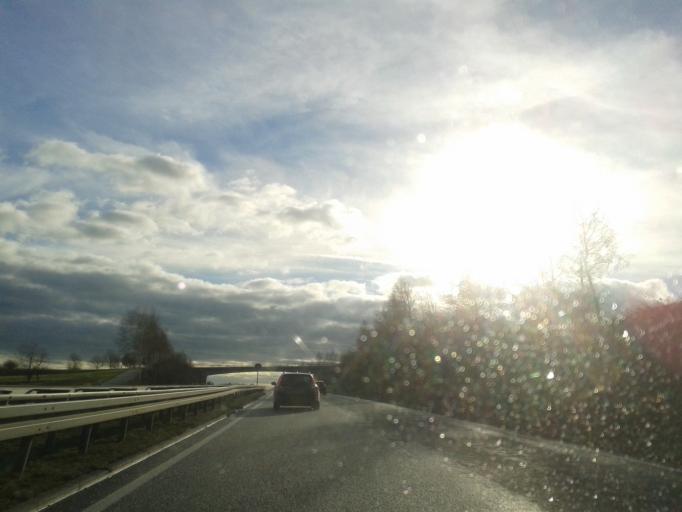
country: DE
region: Saxony
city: Grossschweidnitz
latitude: 51.0936
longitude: 14.6400
